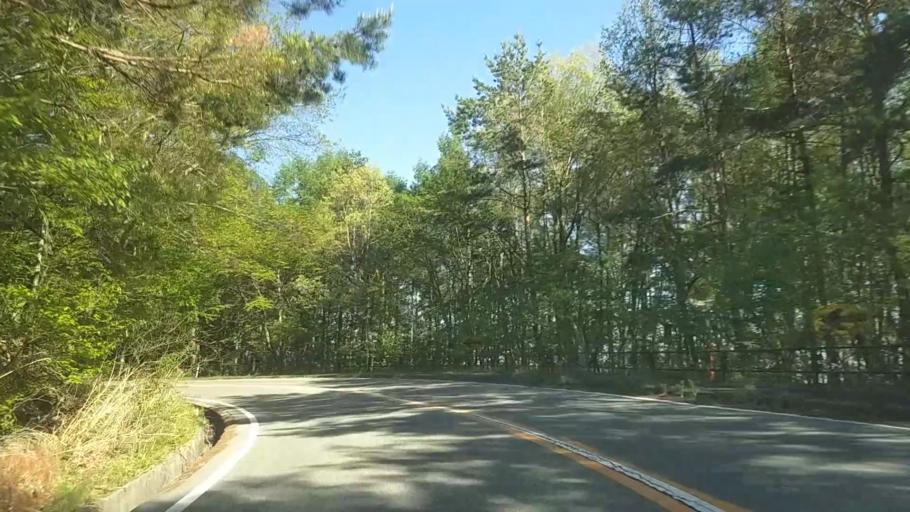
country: JP
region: Yamanashi
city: Nirasaki
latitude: 35.8988
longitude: 138.3600
